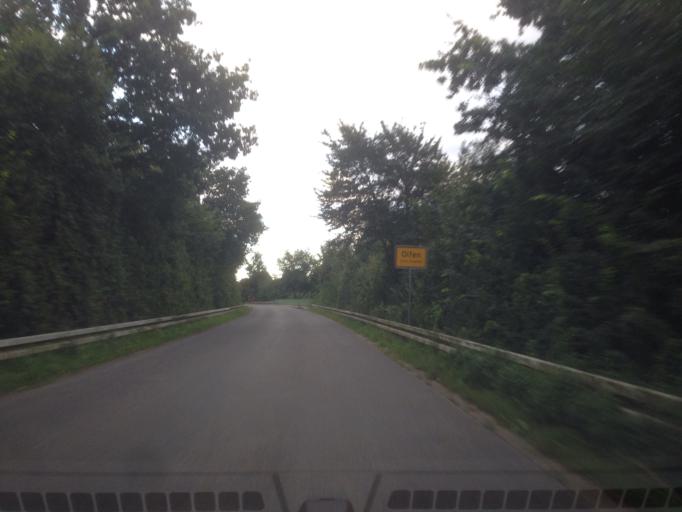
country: DE
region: North Rhine-Westphalia
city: Olfen
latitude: 51.7201
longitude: 7.3768
